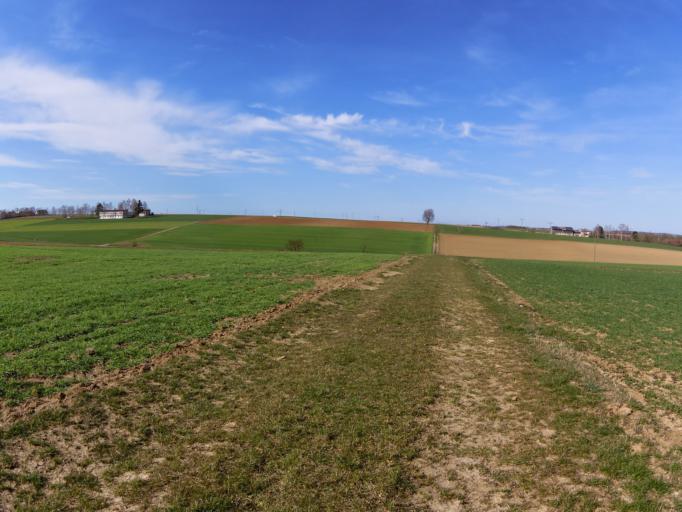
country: DE
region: Bavaria
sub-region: Regierungsbezirk Unterfranken
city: Biebelried
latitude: 49.7940
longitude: 10.0996
